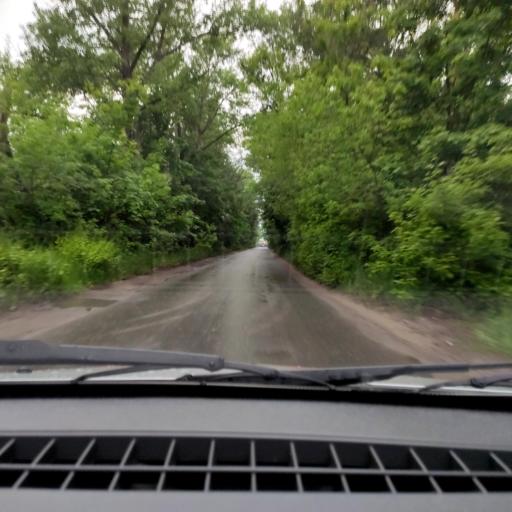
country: RU
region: Voronezj
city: Ramon'
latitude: 51.8481
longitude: 39.2302
